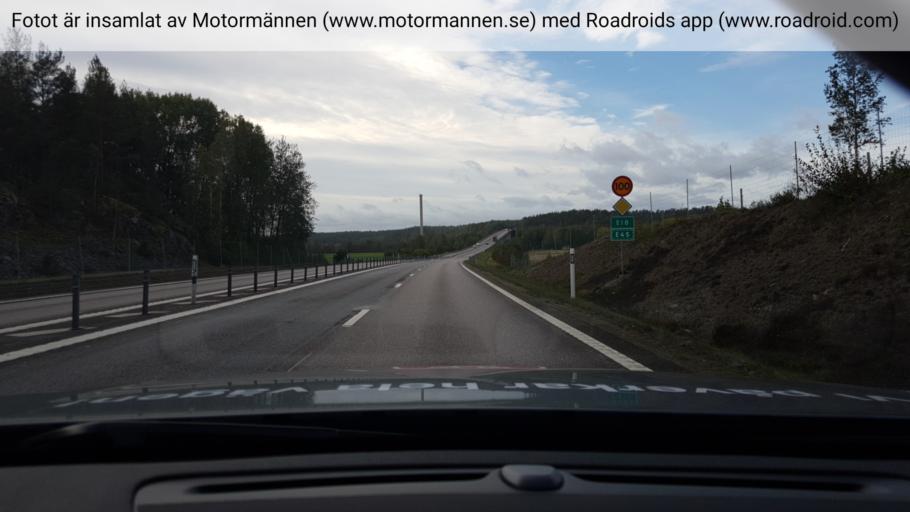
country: SE
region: Vaermland
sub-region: Karlstads Kommun
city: Valberg
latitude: 59.3772
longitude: 13.1965
